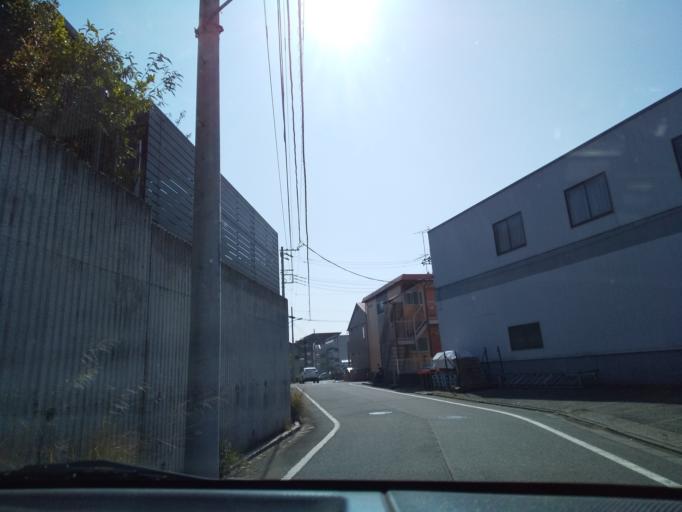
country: JP
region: Tokyo
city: Hino
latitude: 35.6301
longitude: 139.3906
